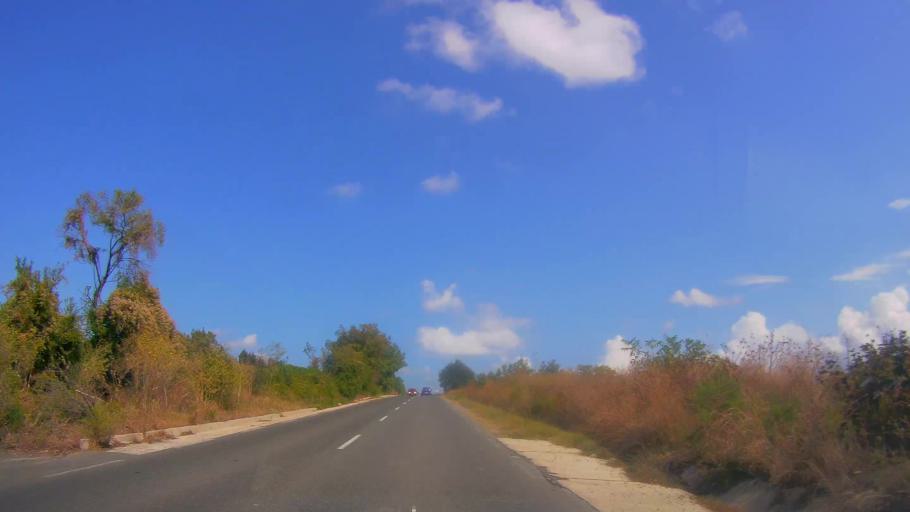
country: BG
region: Burgas
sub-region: Obshtina Burgas
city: Burgas
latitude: 42.4809
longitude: 27.3830
